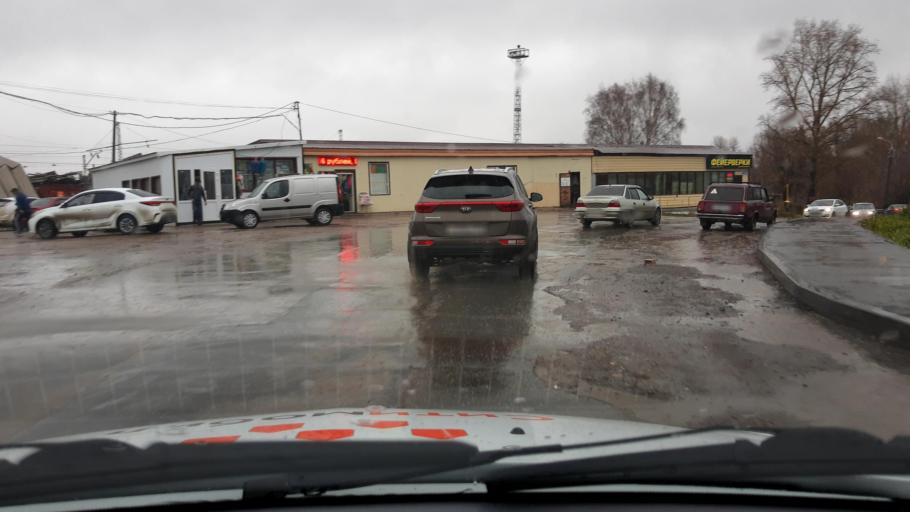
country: RU
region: Bashkortostan
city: Mikhaylovka
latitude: 54.6999
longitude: 55.8491
